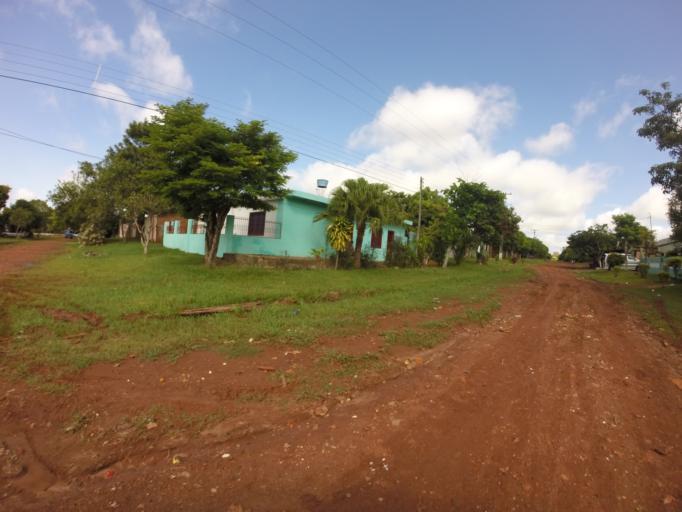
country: PY
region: Alto Parana
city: Ciudad del Este
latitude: -25.4018
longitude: -54.6524
